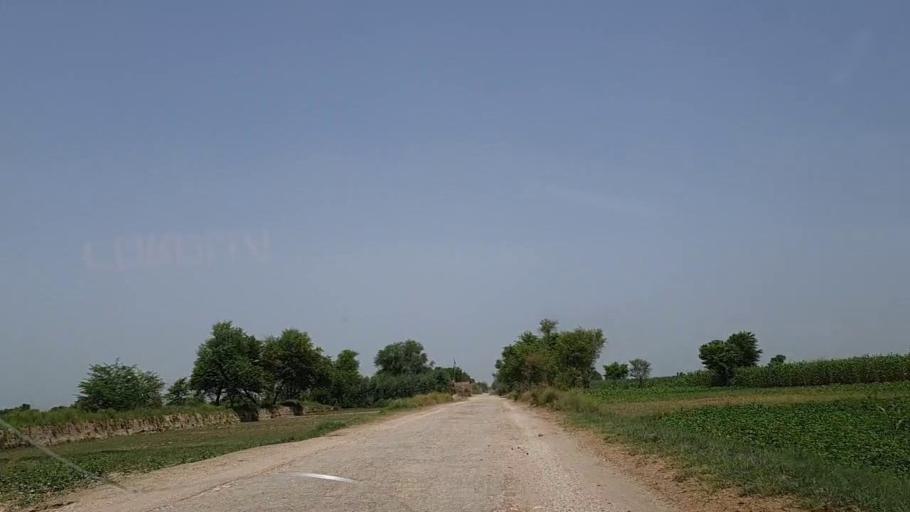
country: PK
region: Sindh
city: Tharu Shah
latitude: 26.9102
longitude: 68.0039
